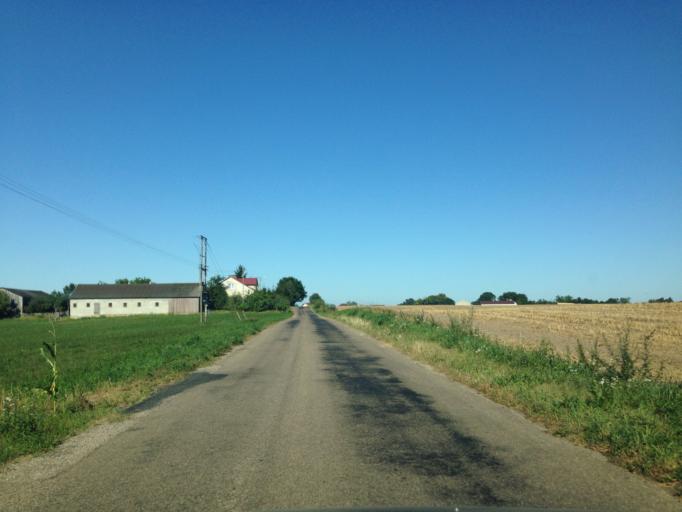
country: PL
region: Kujawsko-Pomorskie
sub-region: Powiat brodnicki
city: Swiedziebnia
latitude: 53.1974
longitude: 19.5380
